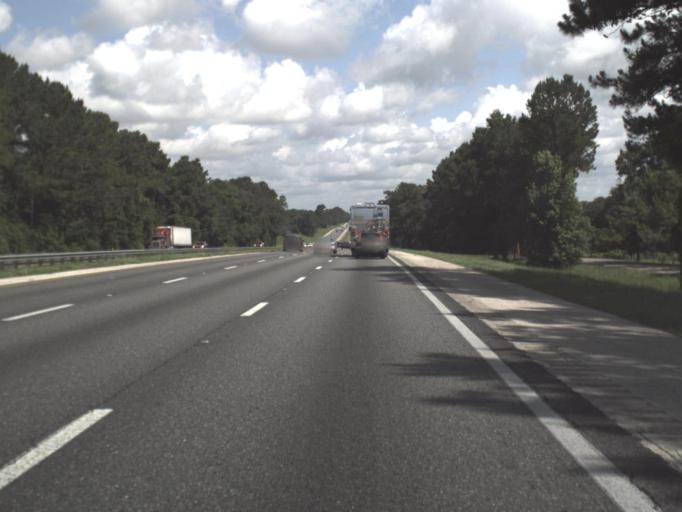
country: US
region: Florida
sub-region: Alachua County
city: High Springs
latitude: 29.8201
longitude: -82.5173
